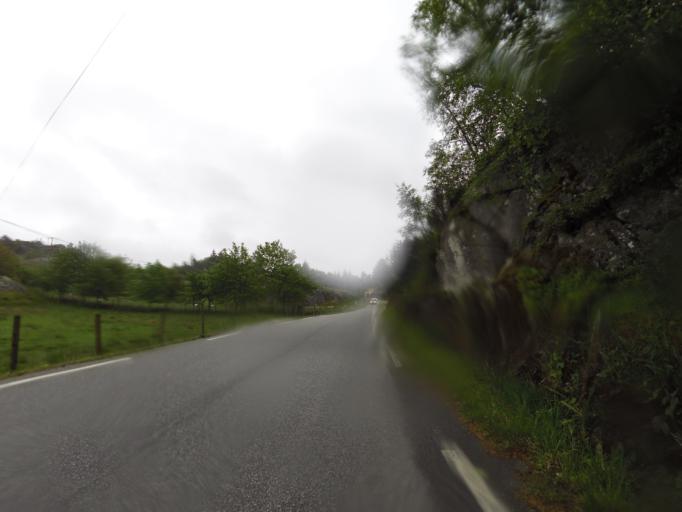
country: NO
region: Hordaland
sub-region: Sveio
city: Sveio
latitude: 59.5250
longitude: 5.2809
